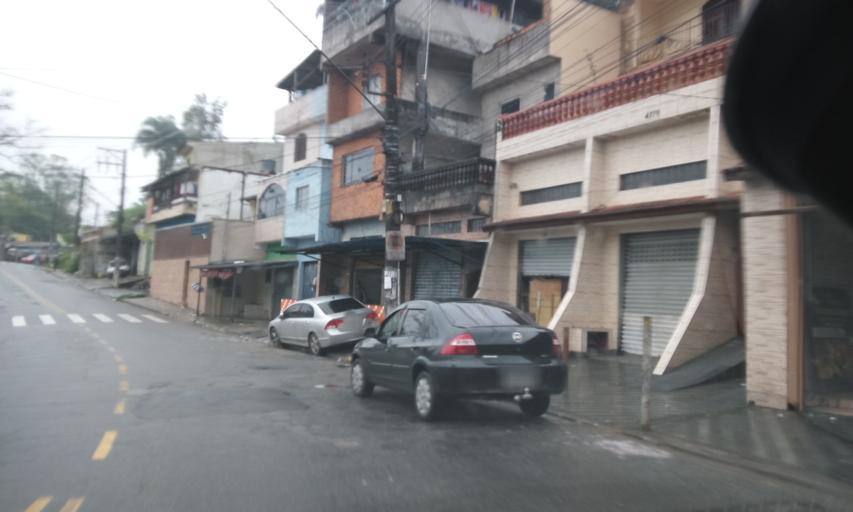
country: BR
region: Sao Paulo
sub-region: Maua
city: Maua
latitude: -23.7365
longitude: -46.4965
